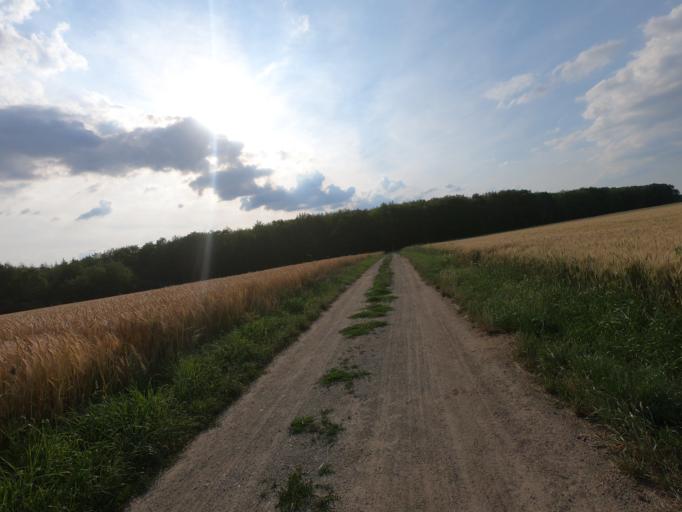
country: DE
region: Hesse
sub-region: Regierungsbezirk Darmstadt
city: Russelsheim
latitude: 49.9629
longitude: 8.4221
